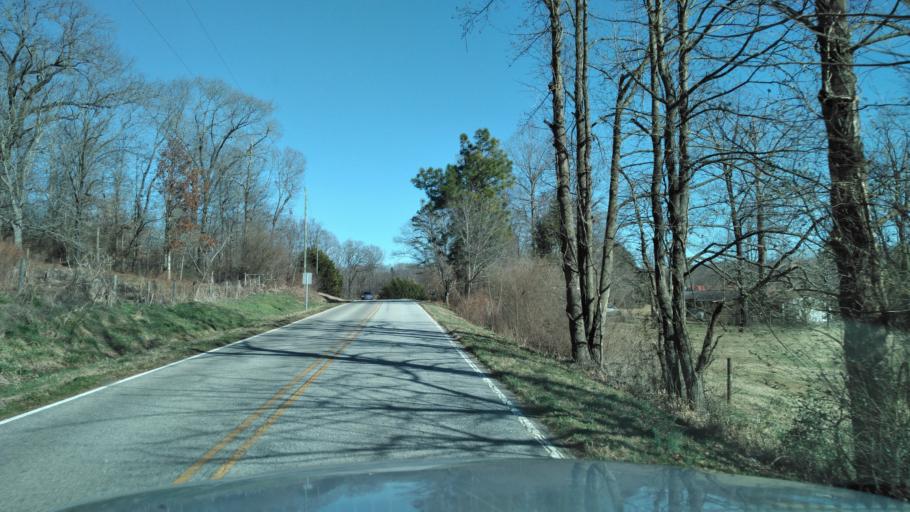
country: US
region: Georgia
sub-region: Hall County
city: Lula
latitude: 34.3187
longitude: -83.6982
